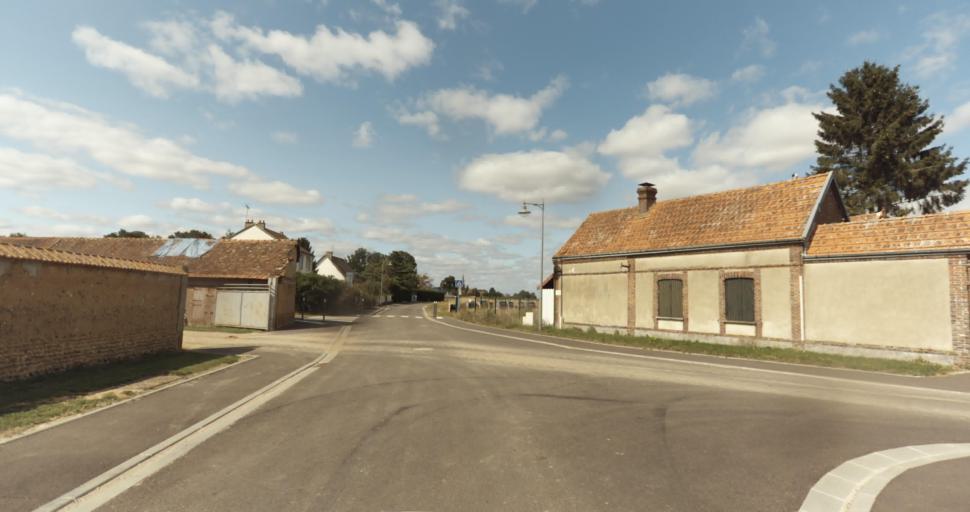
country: FR
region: Haute-Normandie
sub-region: Departement de l'Eure
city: Nonancourt
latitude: 48.8403
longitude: 1.1653
